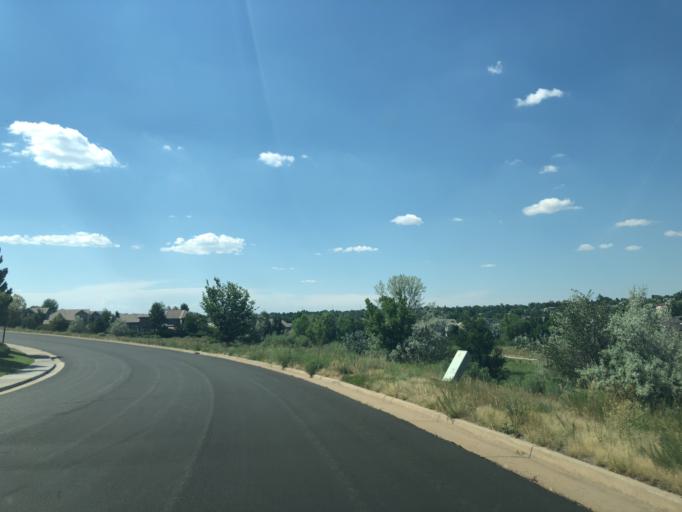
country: US
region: Colorado
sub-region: Arapahoe County
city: Dove Valley
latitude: 39.6057
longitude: -104.7796
